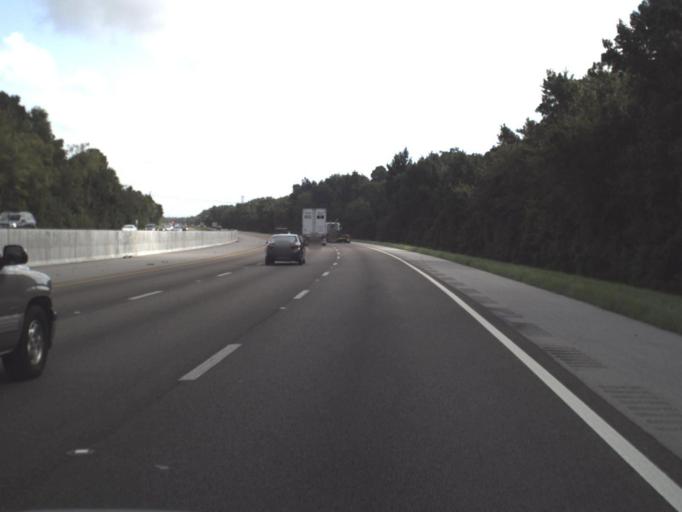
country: US
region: Florida
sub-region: Hillsborough County
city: University
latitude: 28.1109
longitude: -82.4257
